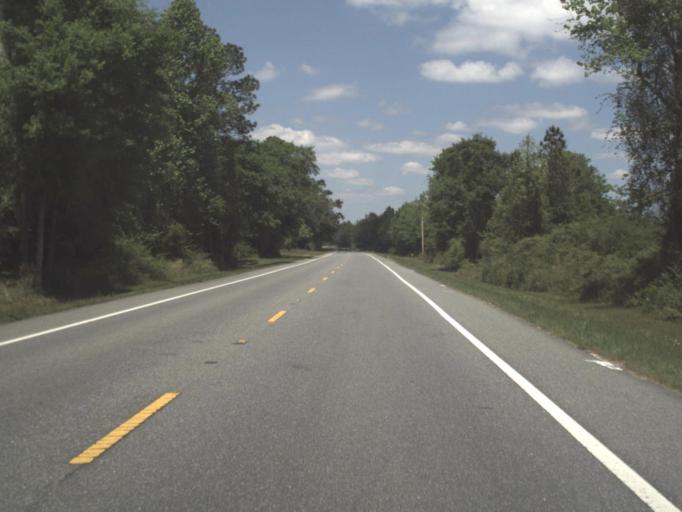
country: US
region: Florida
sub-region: Santa Rosa County
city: Point Baker
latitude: 30.7390
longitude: -87.0431
